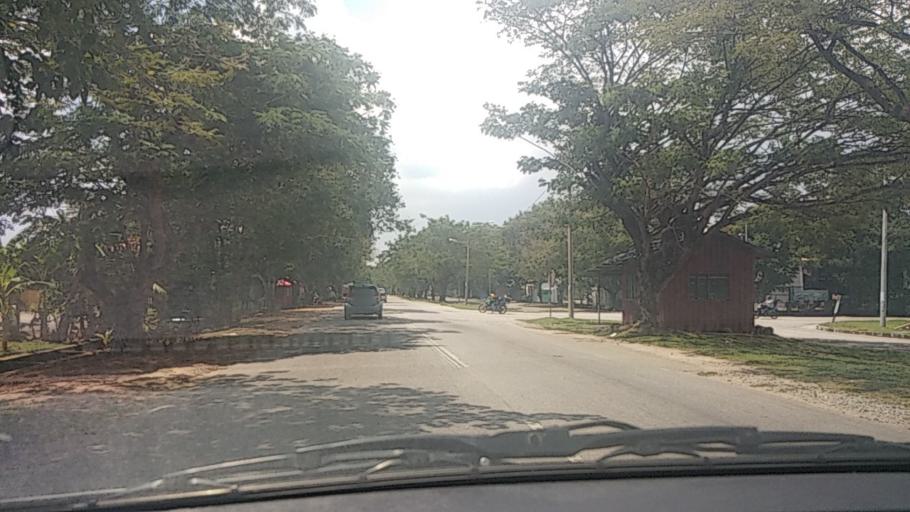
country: MY
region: Kedah
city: Sungai Petani
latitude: 5.6459
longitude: 100.5218
